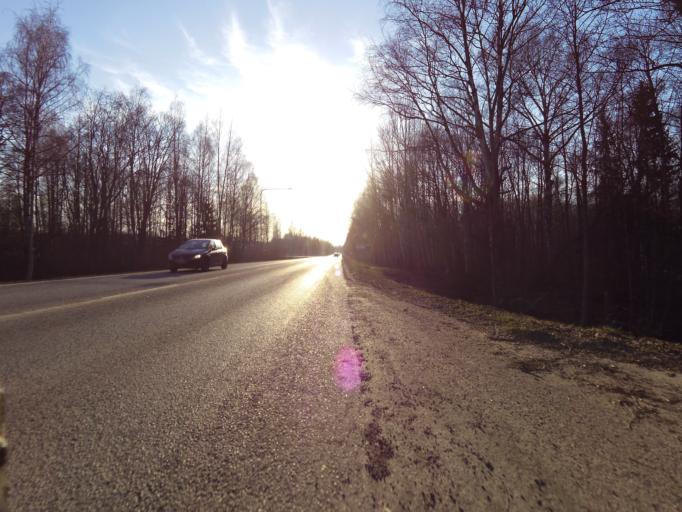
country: SE
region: Gaevleborg
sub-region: Gavle Kommun
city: Gavle
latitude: 60.6742
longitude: 17.2023
